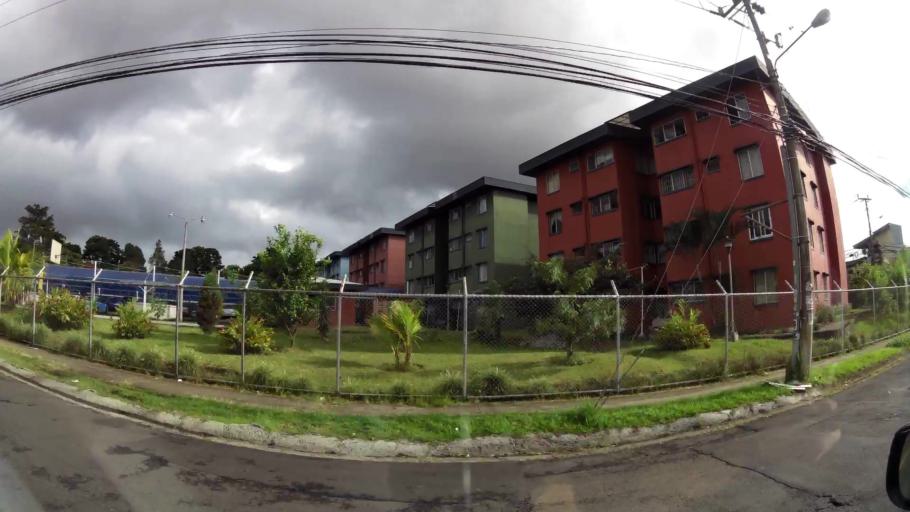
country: CR
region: San Jose
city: Curridabat
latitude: 9.9101
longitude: -84.0430
